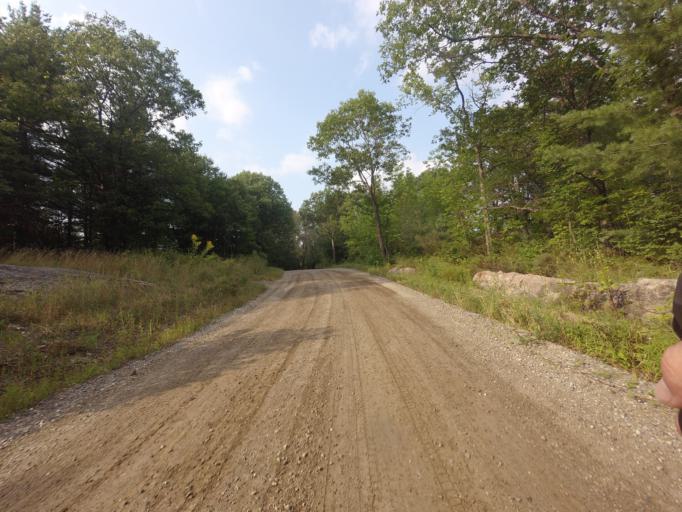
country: CA
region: Ontario
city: Perth
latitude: 44.8640
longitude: -76.7279
